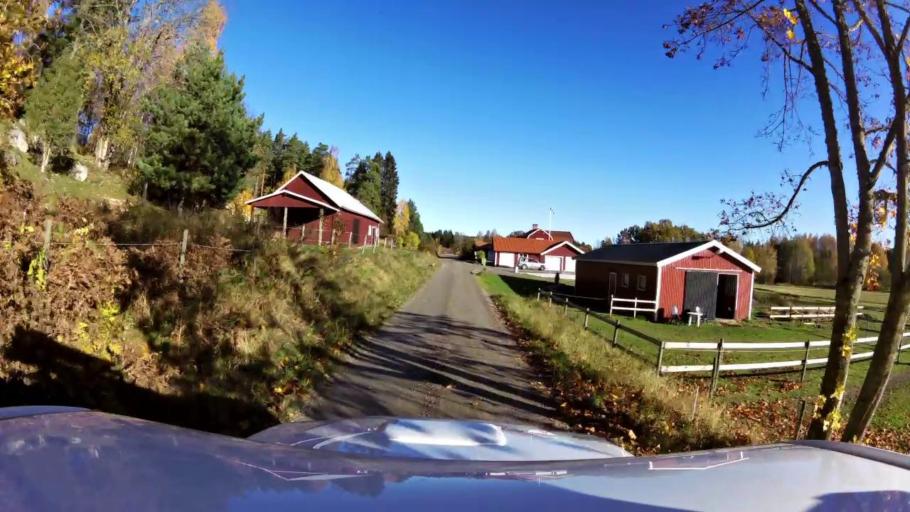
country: SE
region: OEstergoetland
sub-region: Linkopings Kommun
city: Ljungsbro
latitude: 58.5264
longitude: 15.4918
